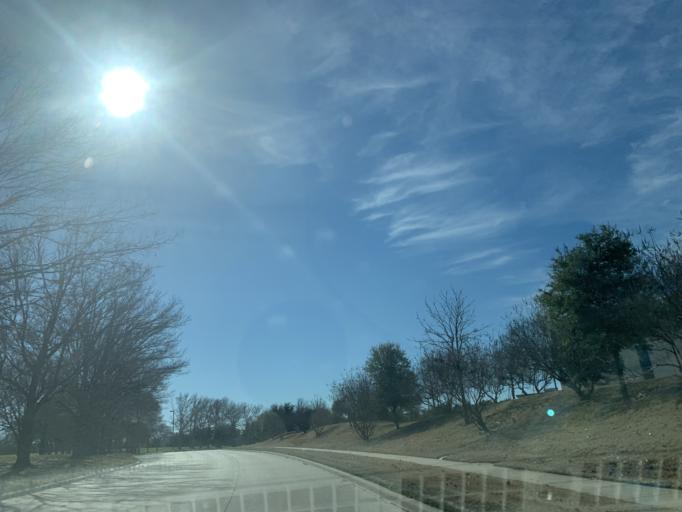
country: US
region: Texas
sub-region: Denton County
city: The Colony
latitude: 33.0839
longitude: -96.8352
